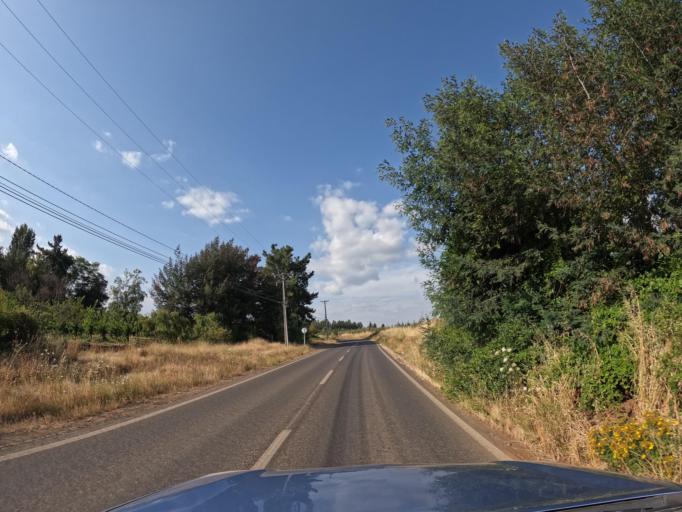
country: CL
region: Maule
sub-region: Provincia de Curico
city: Molina
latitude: -35.2641
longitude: -71.2446
